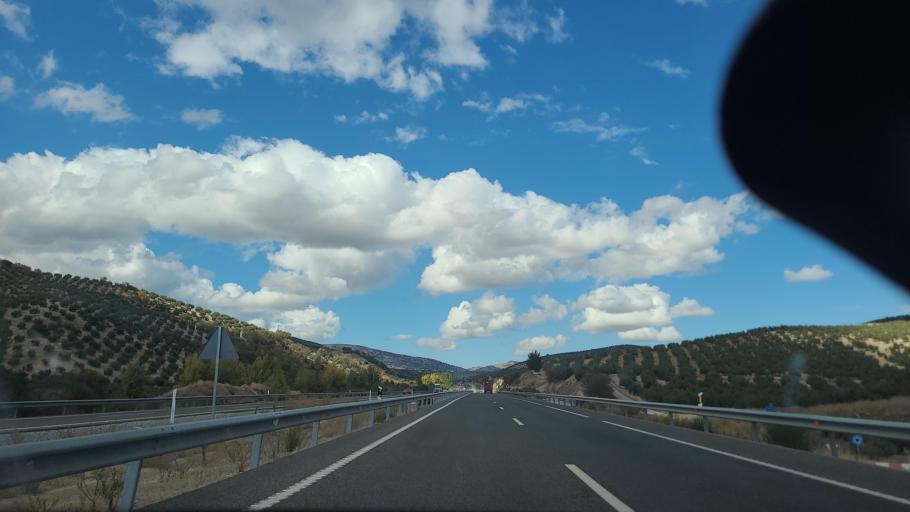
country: ES
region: Andalusia
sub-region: Provincia de Granada
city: Campotejar
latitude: 37.4947
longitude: -3.6244
